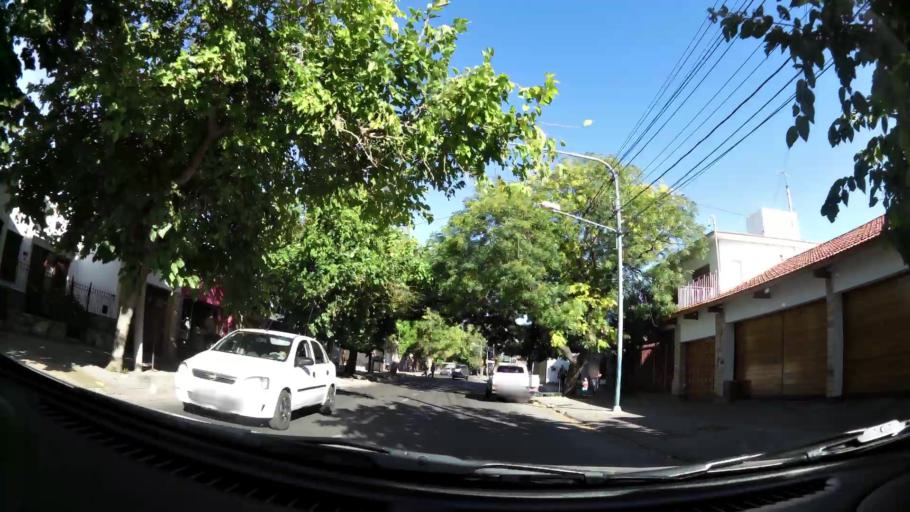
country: AR
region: Mendoza
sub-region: Departamento de Godoy Cruz
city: Godoy Cruz
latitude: -32.9302
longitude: -68.8409
